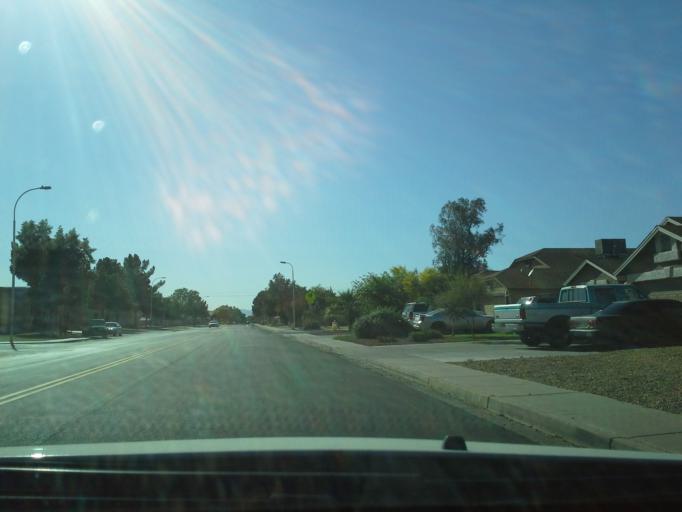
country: US
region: Arizona
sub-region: Maricopa County
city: Glendale
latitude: 33.5310
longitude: -112.2082
